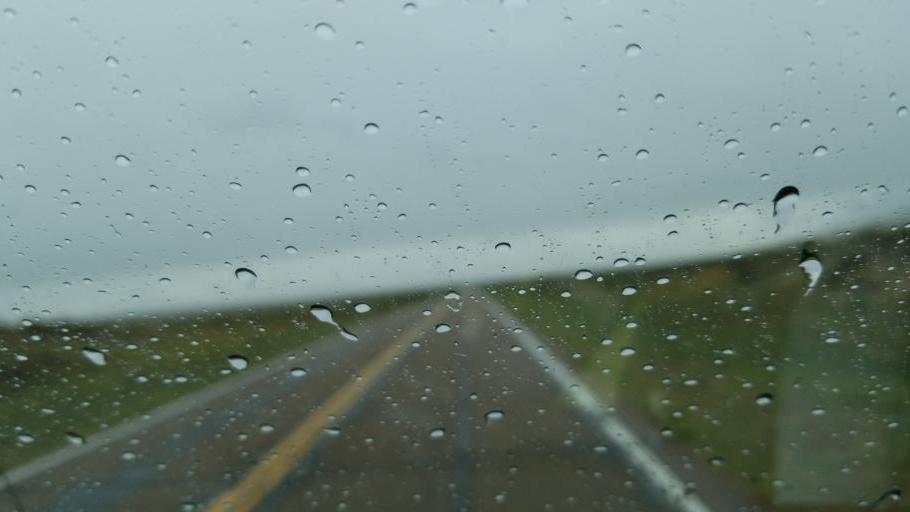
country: US
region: Colorado
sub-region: Lincoln County
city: Hugo
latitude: 38.8496
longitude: -103.1704
